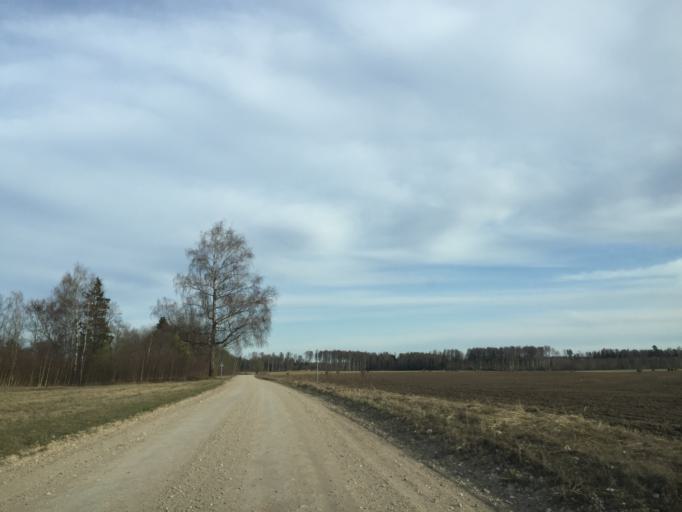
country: LV
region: Kegums
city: Kegums
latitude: 56.7974
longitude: 24.7517
